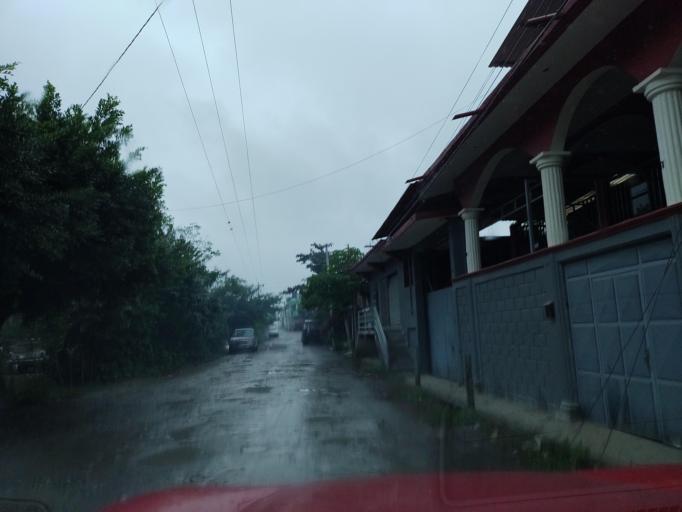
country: MX
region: Veracruz
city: Agua Dulce
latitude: 20.3626
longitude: -97.3301
